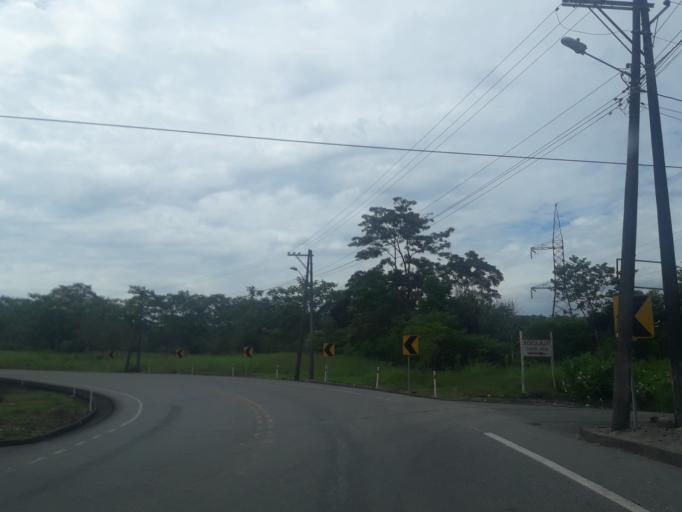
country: EC
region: Napo
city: Tena
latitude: -1.0479
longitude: -77.7961
